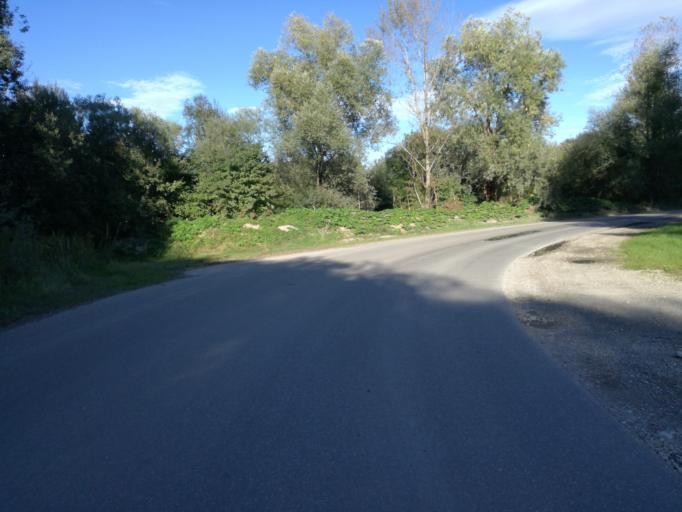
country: DE
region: Bavaria
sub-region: Upper Bavaria
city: Planegg
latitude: 48.0985
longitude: 11.4349
